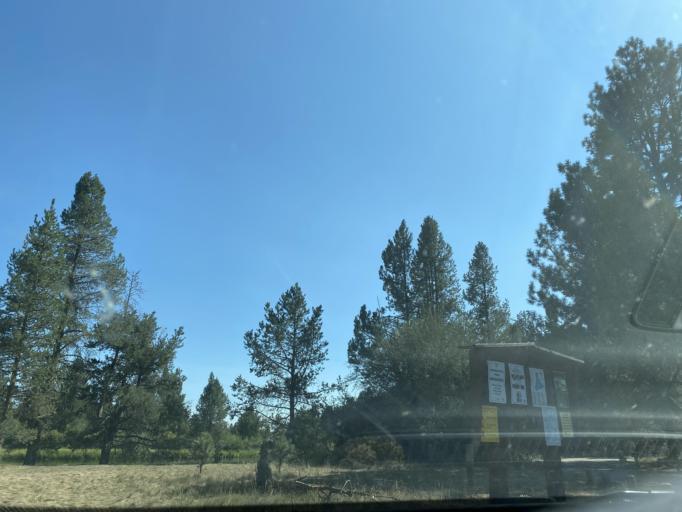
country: US
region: Oregon
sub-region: Deschutes County
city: Sunriver
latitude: 43.8807
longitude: -121.4629
